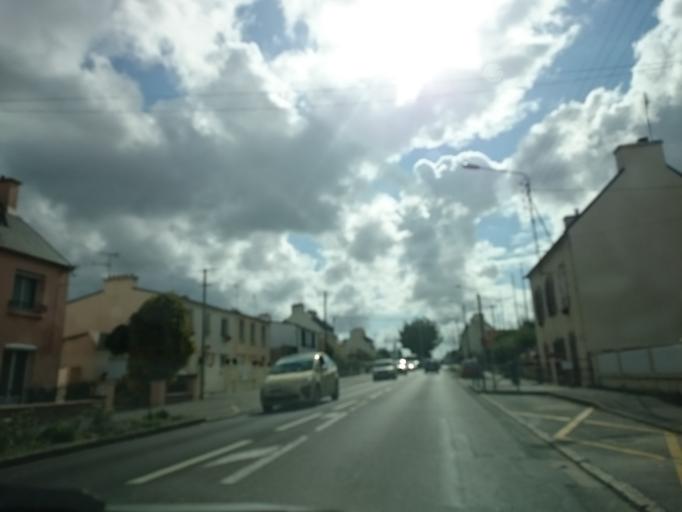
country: FR
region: Brittany
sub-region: Departement du Finistere
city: Brest
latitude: 48.4136
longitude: -4.4477
